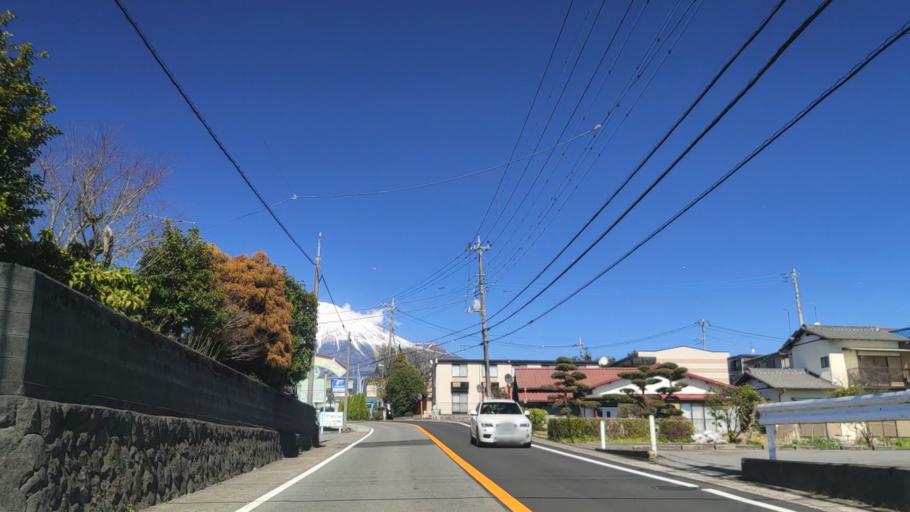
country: JP
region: Shizuoka
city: Fujinomiya
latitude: 35.2138
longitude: 138.6370
